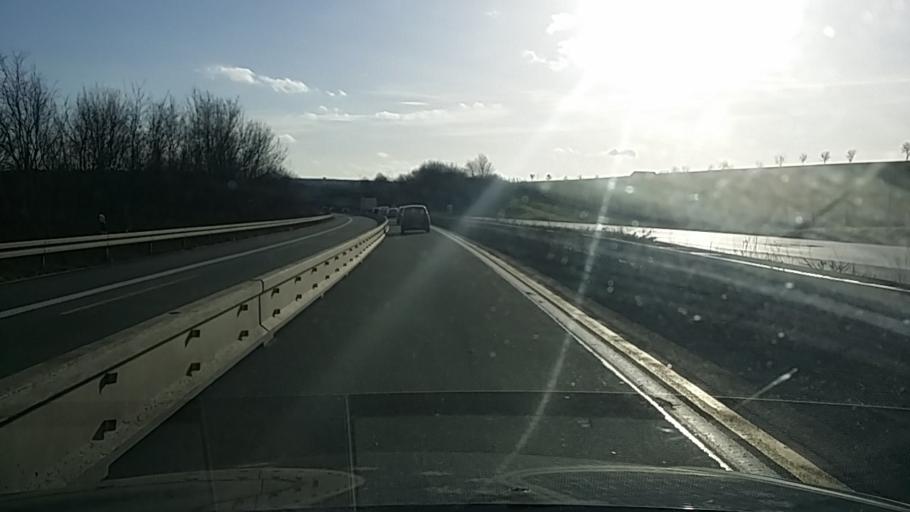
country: DE
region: North Rhine-Westphalia
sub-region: Regierungsbezirk Detmold
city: Paderborn
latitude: 51.6610
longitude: 8.7076
